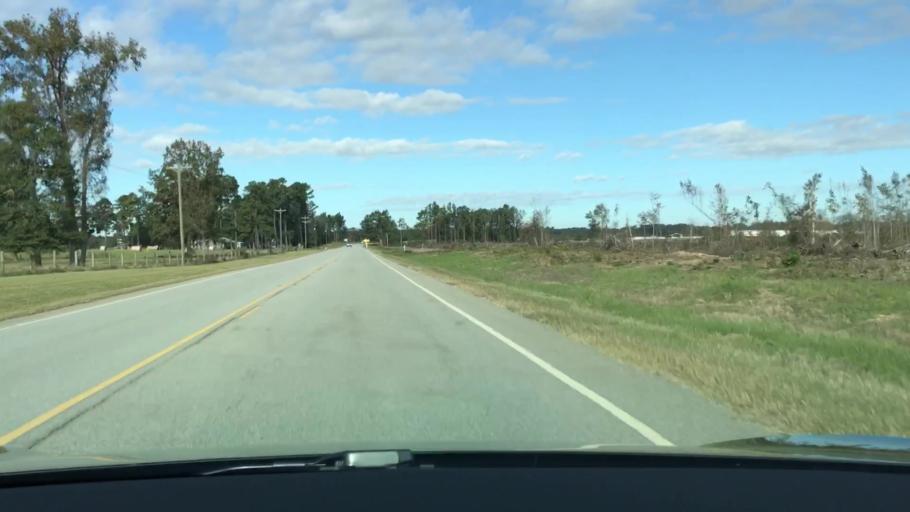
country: US
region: Georgia
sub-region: Jefferson County
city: Wrens
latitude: 33.1204
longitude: -82.4446
